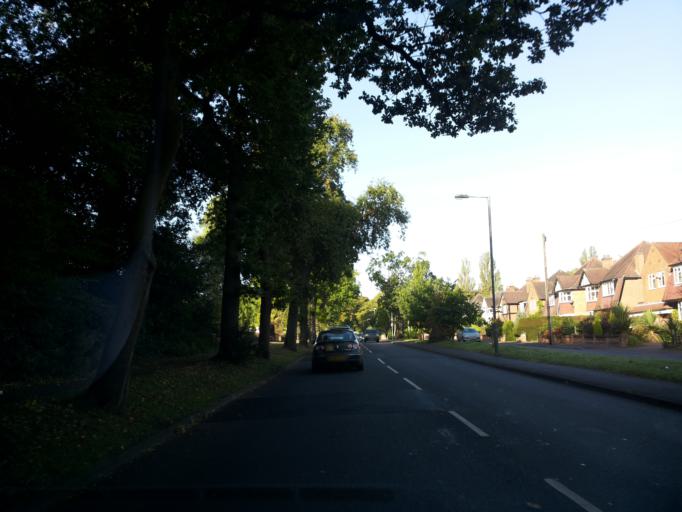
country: GB
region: England
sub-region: Solihull
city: Shirley
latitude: 52.4207
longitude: -1.8101
